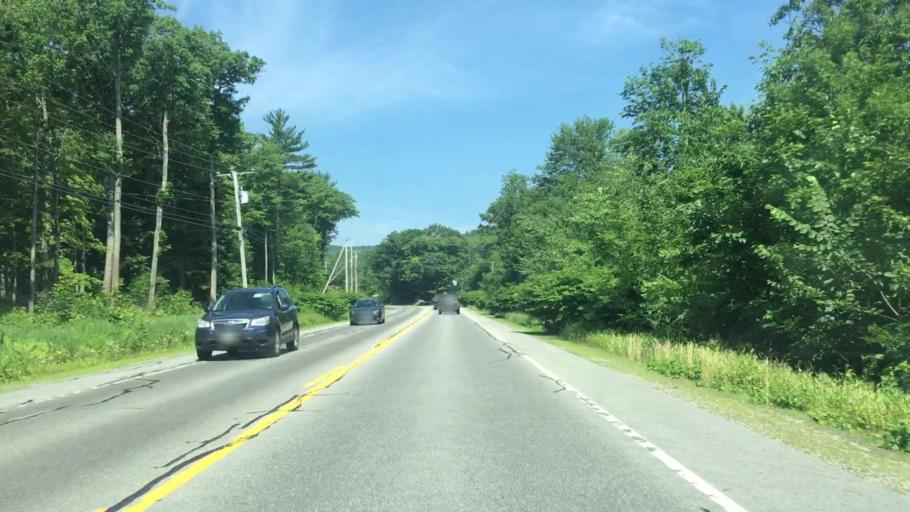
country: US
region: New Hampshire
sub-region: Merrimack County
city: Newbury
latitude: 43.3098
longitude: -72.0189
